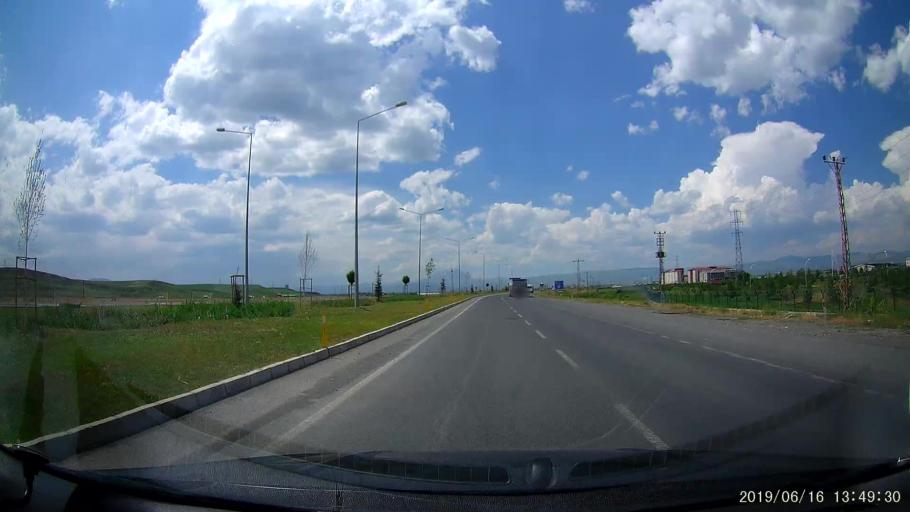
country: TR
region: Agri
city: Agri
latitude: 39.7178
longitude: 42.9900
